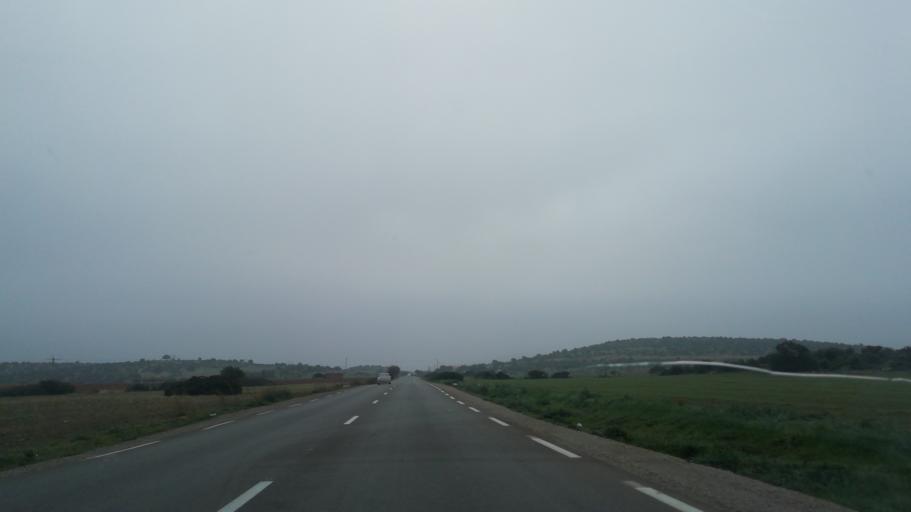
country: DZ
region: Mascara
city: Oued el Abtal
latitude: 35.2972
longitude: 0.4525
